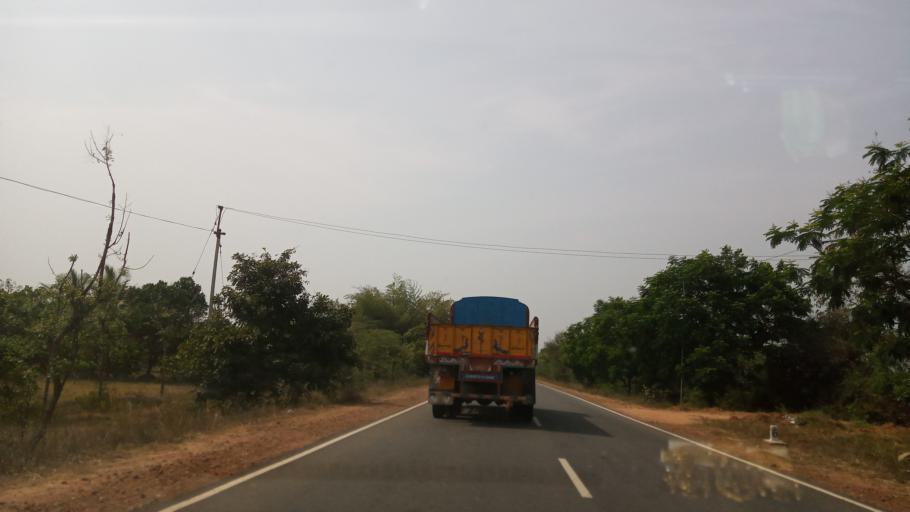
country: IN
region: Tamil Nadu
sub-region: Cuddalore
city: Srimushnam
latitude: 11.3959
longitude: 79.3606
